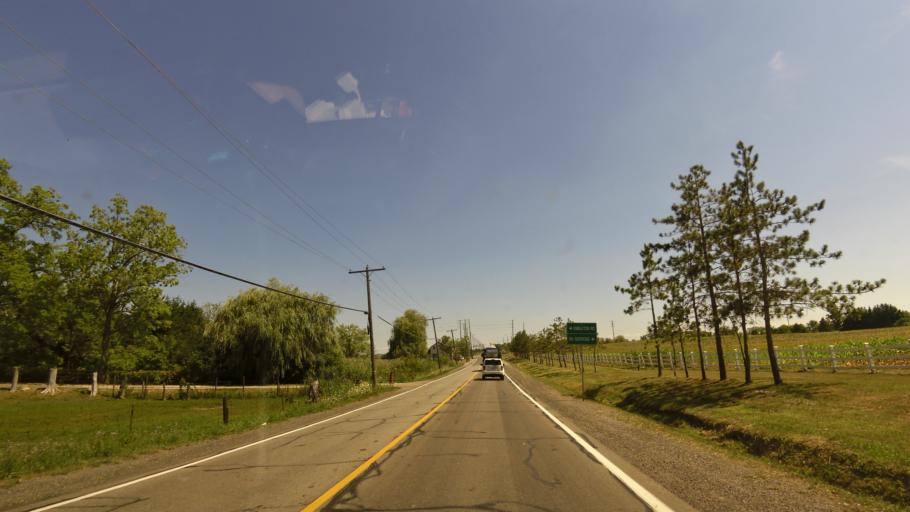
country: CA
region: Ontario
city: Brampton
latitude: 43.6289
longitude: -79.8268
